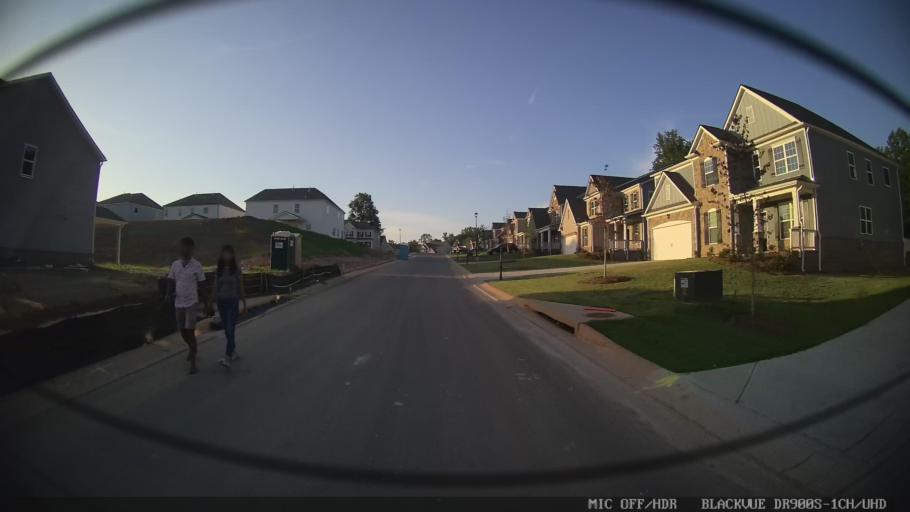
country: US
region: Georgia
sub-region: Forsyth County
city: Cumming
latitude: 34.2176
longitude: -84.2063
